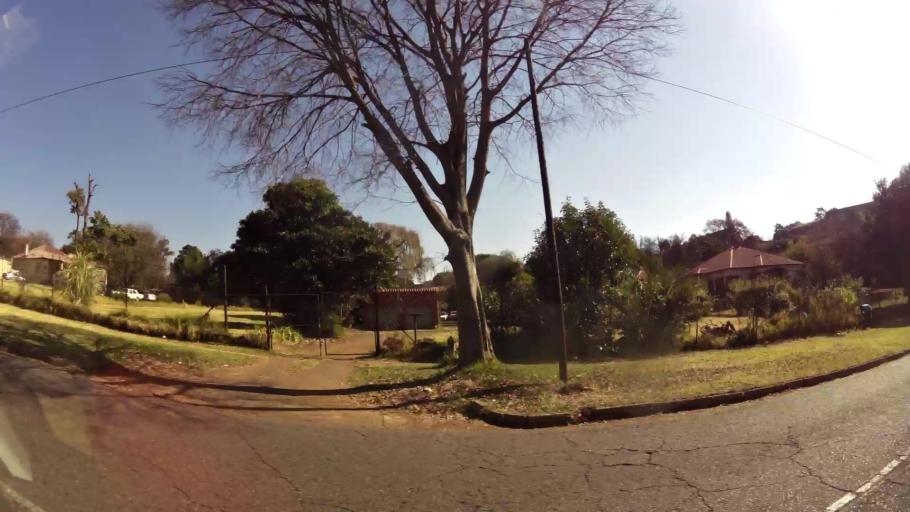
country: ZA
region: Gauteng
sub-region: City of Johannesburg Metropolitan Municipality
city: Johannesburg
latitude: -26.1792
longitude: 28.0751
